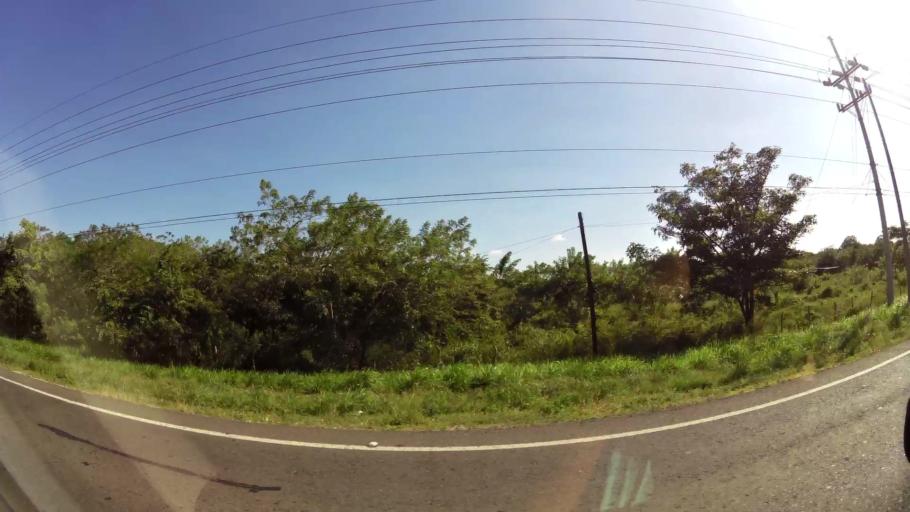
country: CR
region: Guanacaste
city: Liberia
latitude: 10.6165
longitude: -85.4698
